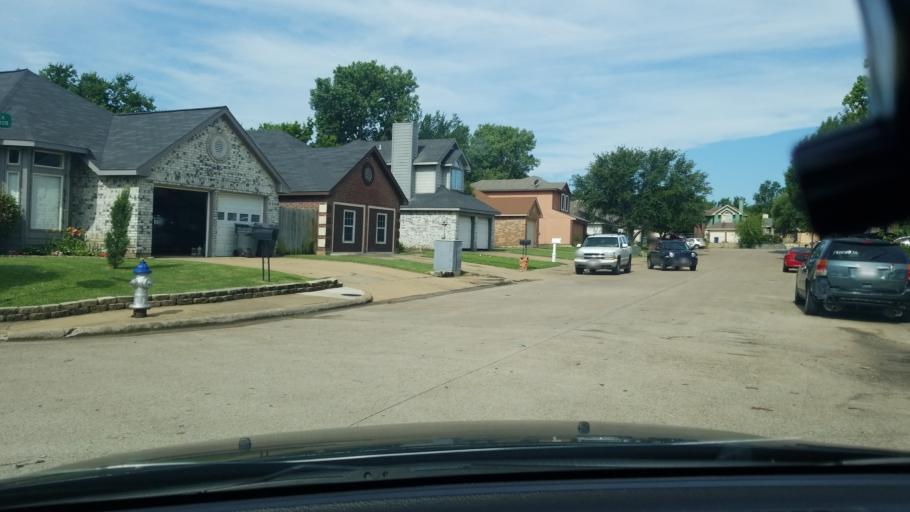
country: US
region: Texas
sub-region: Dallas County
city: Balch Springs
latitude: 32.7697
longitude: -96.6594
